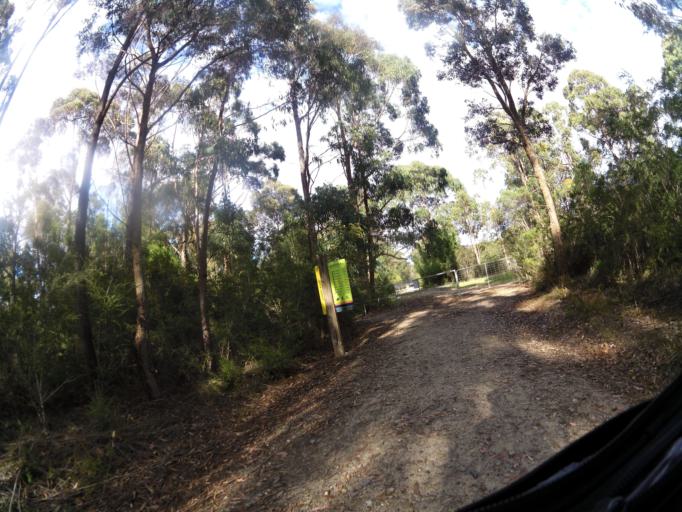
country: AU
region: Victoria
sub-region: East Gippsland
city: Lakes Entrance
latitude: -37.7448
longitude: 148.3824
